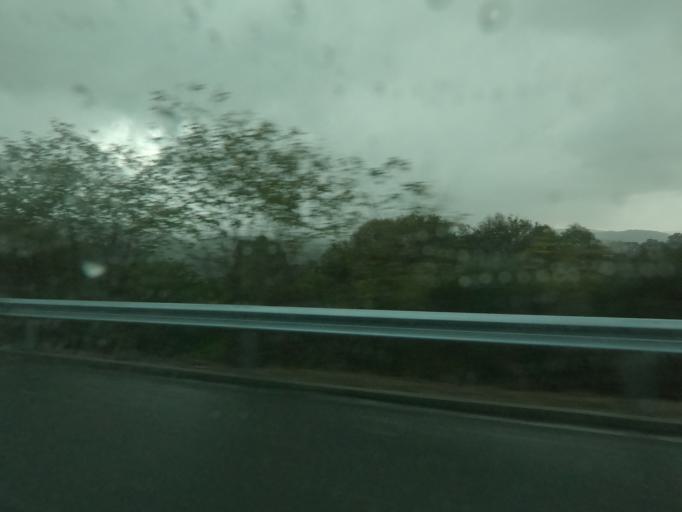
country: ES
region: Galicia
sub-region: Provincia de Pontevedra
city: Marin
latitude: 42.3512
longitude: -8.6460
